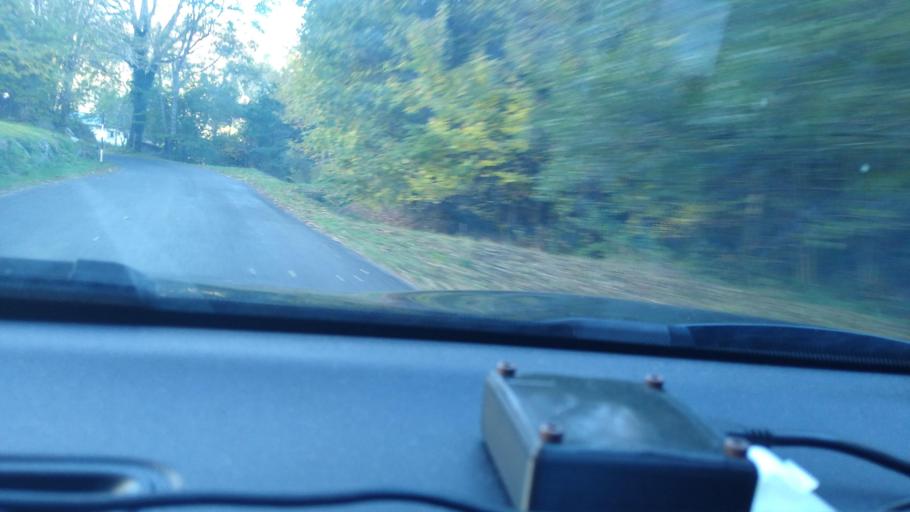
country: FR
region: Languedoc-Roussillon
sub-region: Departement de l'Aude
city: Quillan
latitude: 42.7418
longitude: 2.1940
